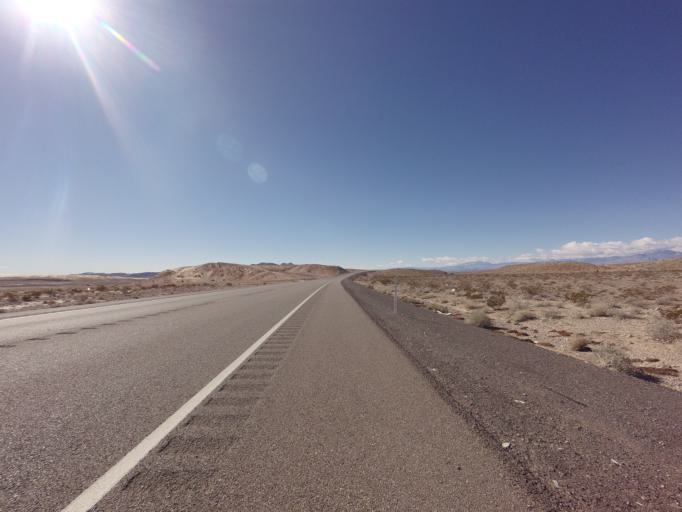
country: US
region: Nevada
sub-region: Clark County
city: Nellis Air Force Base
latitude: 36.3048
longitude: -114.9543
